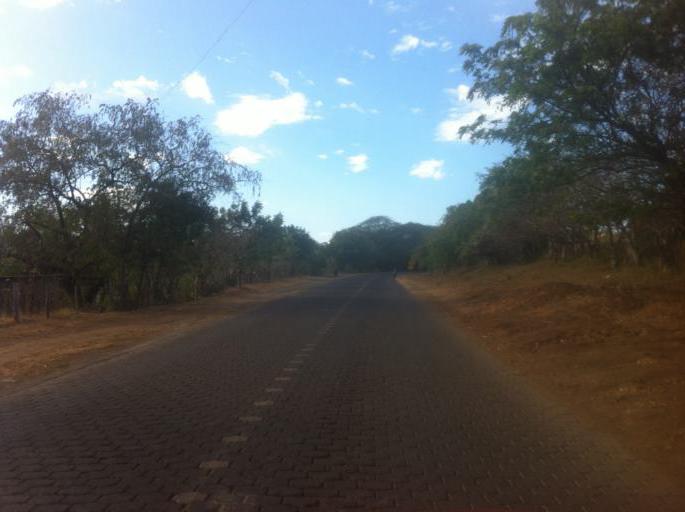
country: NI
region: Managua
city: Masachapa
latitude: 11.8318
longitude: -86.5079
